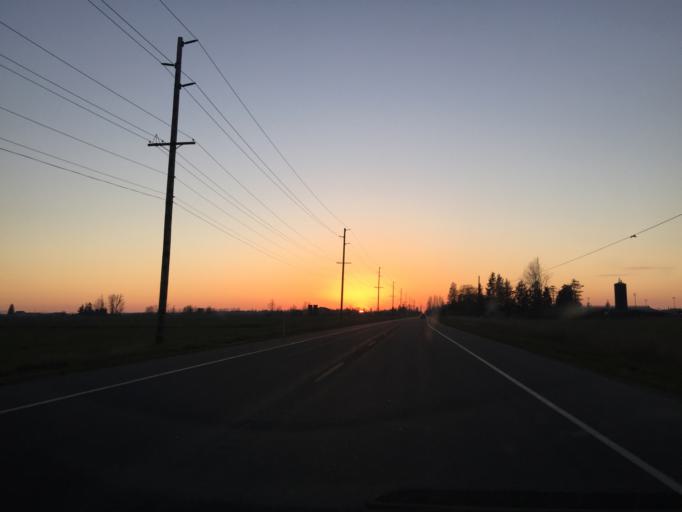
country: US
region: Washington
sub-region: Whatcom County
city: Nooksack
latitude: 48.9639
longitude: -122.2967
